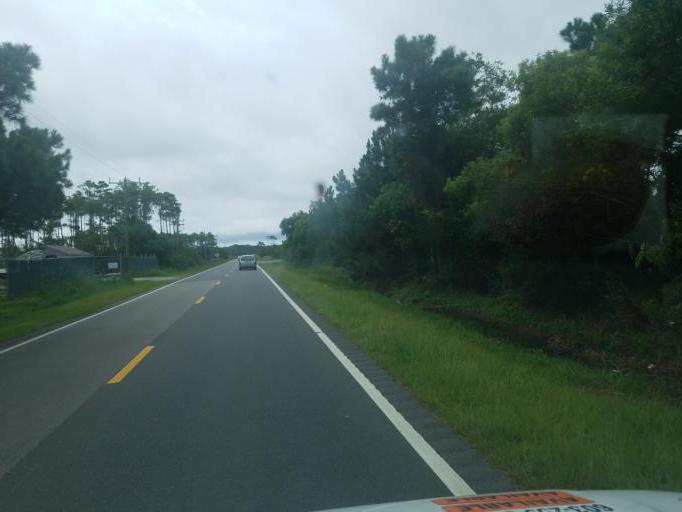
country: US
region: North Carolina
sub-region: Dare County
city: Wanchese
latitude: 35.8620
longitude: -75.6477
